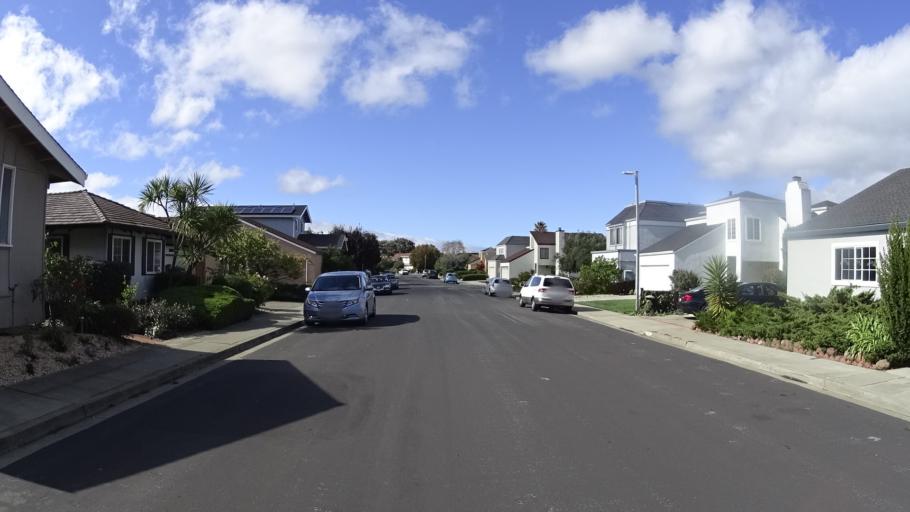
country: US
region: California
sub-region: San Mateo County
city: Foster City
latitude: 37.5663
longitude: -122.2622
